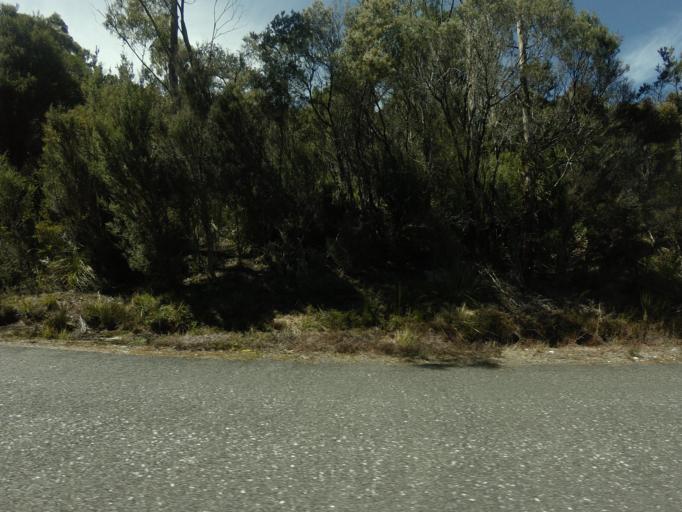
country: AU
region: Tasmania
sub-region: West Coast
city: Queenstown
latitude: -42.7742
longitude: 146.0574
